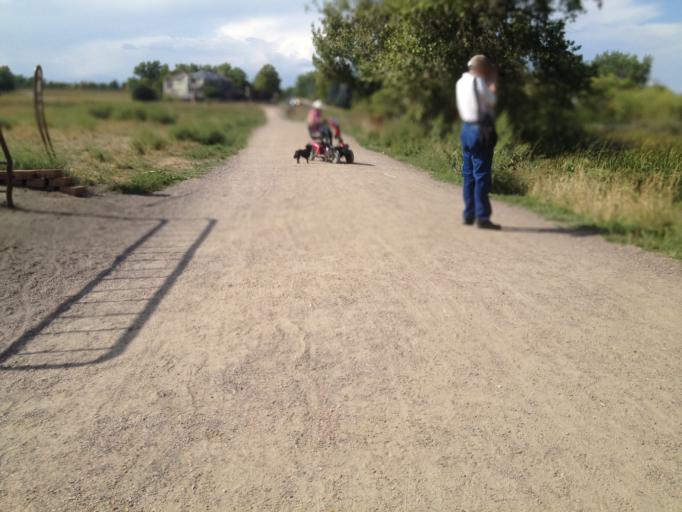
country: US
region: Colorado
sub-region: Boulder County
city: Louisville
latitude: 39.9938
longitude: -105.1158
